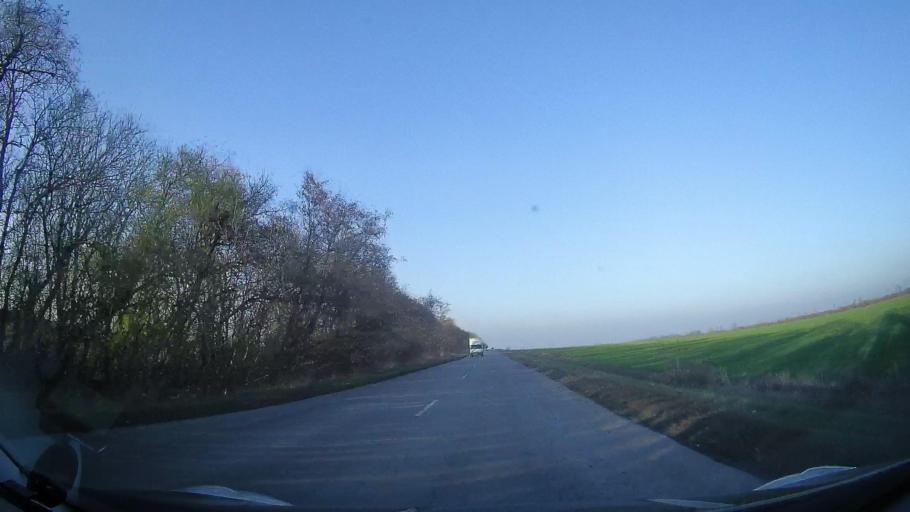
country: RU
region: Rostov
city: Kirovskaya
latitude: 47.0068
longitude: 39.9790
